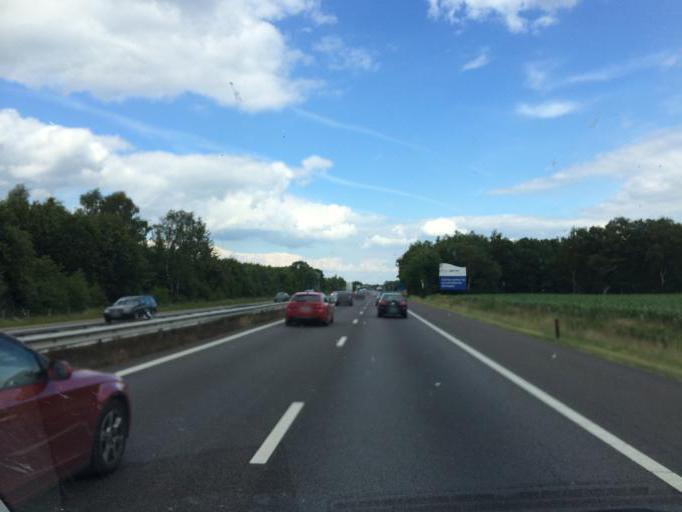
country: NL
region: North Brabant
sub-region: Gemeente Geldrop-Mierlo
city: Geldrop
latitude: 51.4049
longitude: 5.5273
